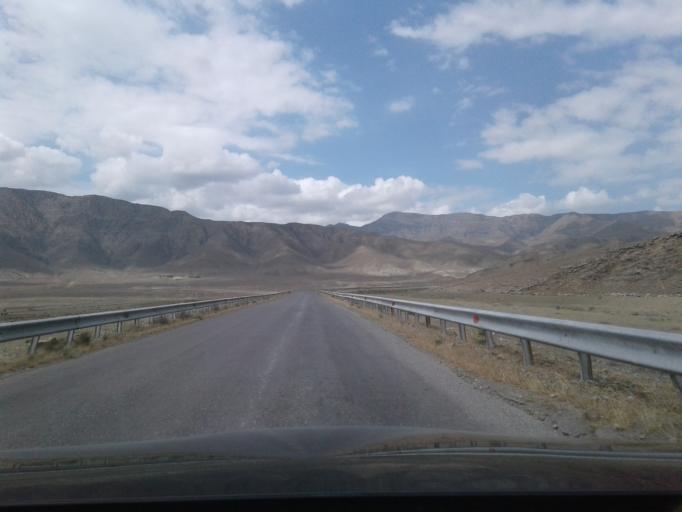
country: TM
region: Ahal
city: Baharly
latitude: 38.5048
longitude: 57.1246
